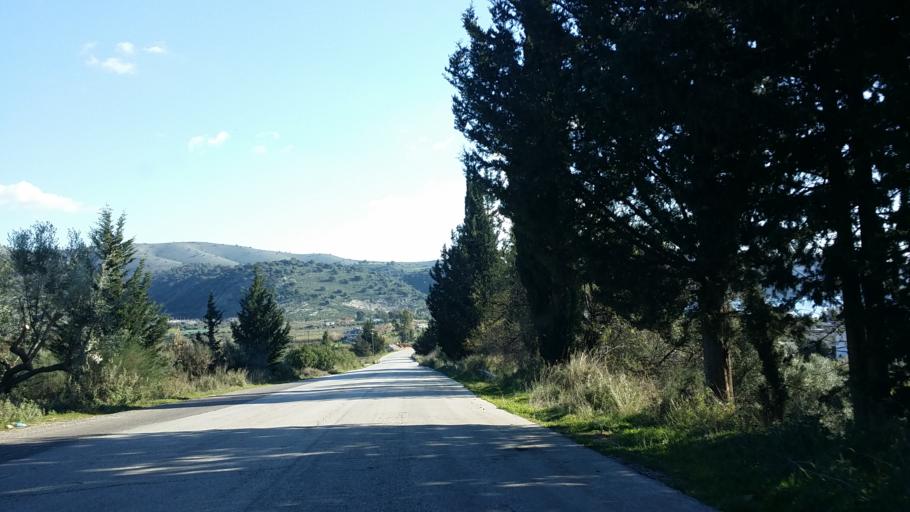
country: GR
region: West Greece
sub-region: Nomos Aitolias kai Akarnanias
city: Astakos
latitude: 38.5409
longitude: 21.0874
